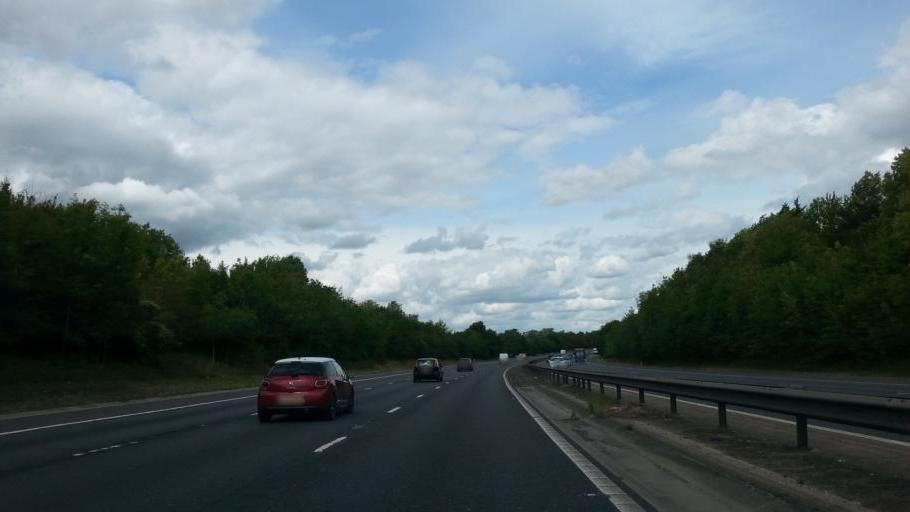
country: GB
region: England
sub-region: Hertfordshire
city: Sawbridgeworth
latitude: 51.8044
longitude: 0.1761
